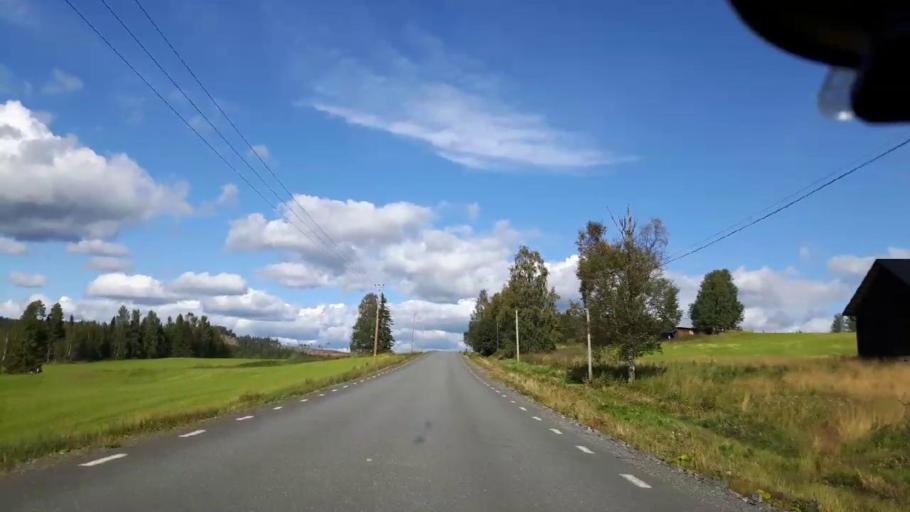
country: SE
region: Jaemtland
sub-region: Braecke Kommun
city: Braecke
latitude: 63.1861
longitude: 15.5593
